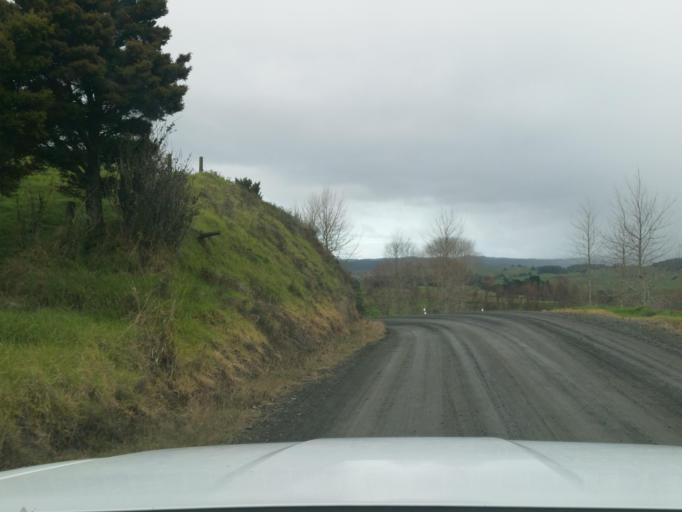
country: NZ
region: Northland
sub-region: Kaipara District
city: Dargaville
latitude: -35.8159
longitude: 173.8029
